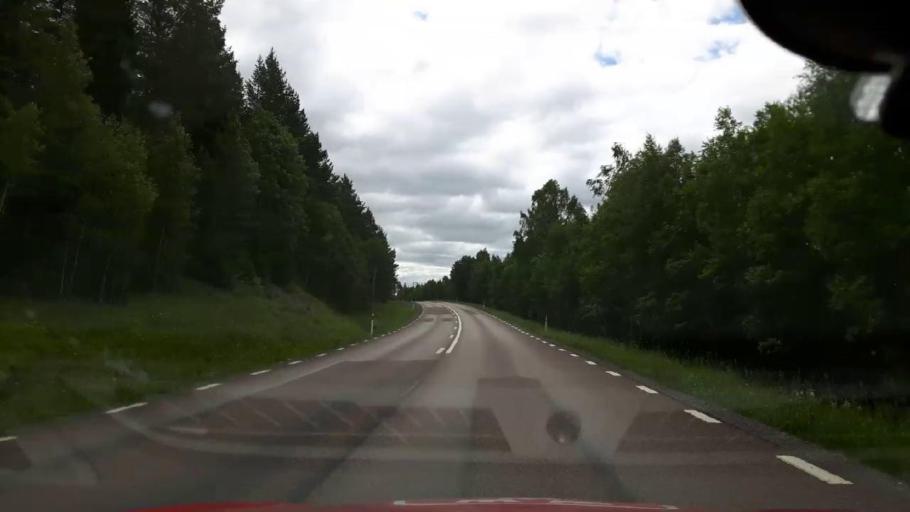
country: SE
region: Jaemtland
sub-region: OEstersunds Kommun
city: Brunflo
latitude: 62.9667
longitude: 15.0218
